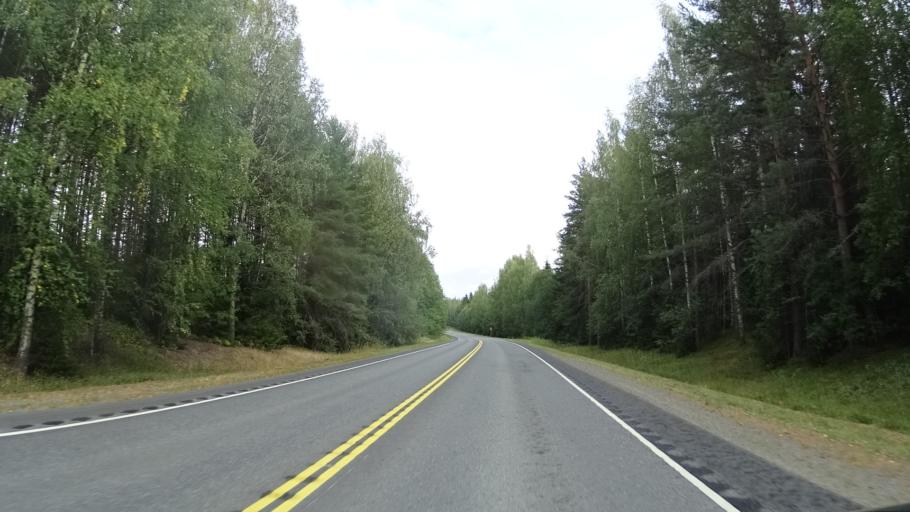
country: FI
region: Haeme
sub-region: Haemeenlinna
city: Parola
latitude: 61.0268
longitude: 24.2901
